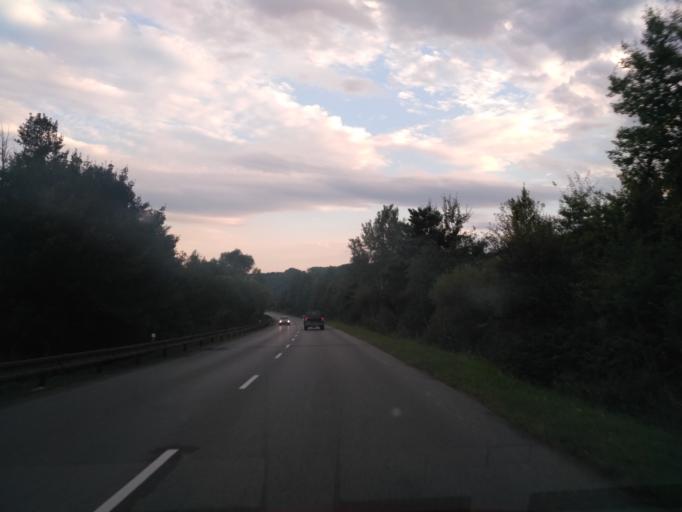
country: SK
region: Presovsky
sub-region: Okres Presov
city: Presov
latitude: 48.9590
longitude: 21.1630
